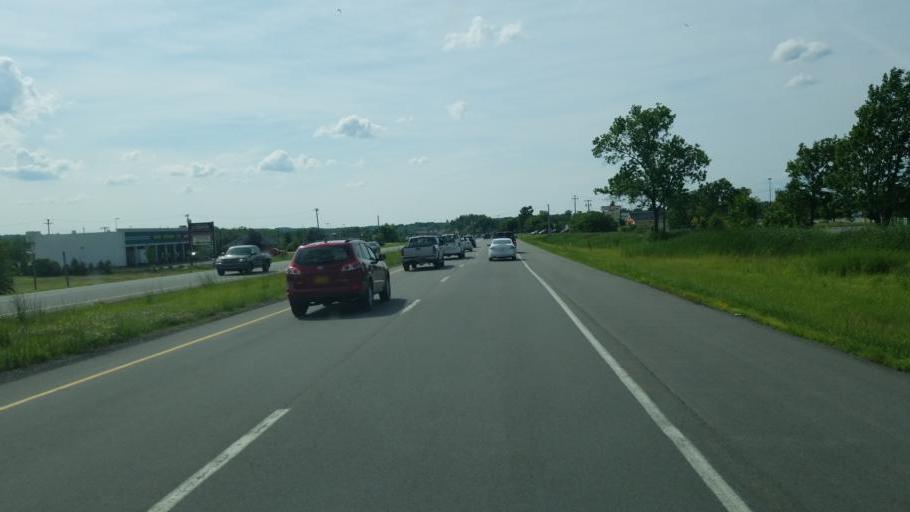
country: US
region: New York
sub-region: Ontario County
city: Canandaigua
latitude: 42.8737
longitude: -77.2431
